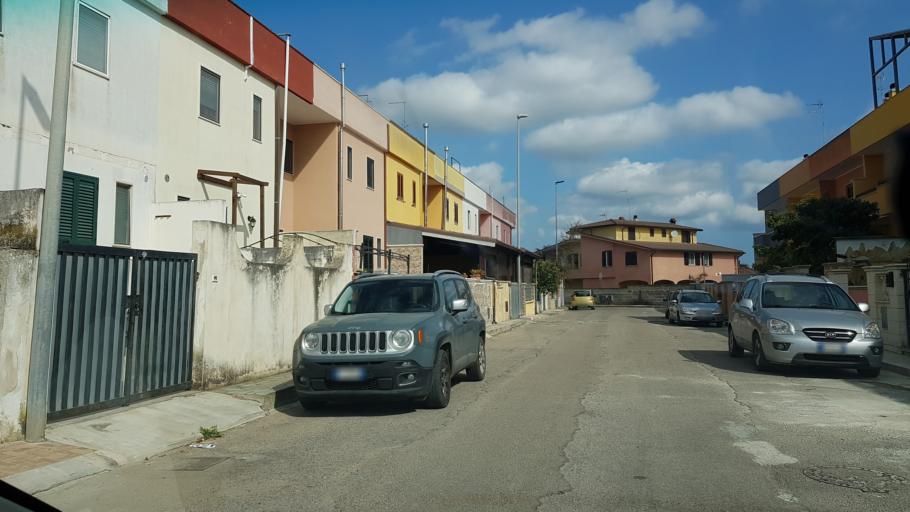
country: IT
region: Apulia
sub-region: Provincia di Brindisi
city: San Pietro Vernotico
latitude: 40.4781
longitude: 17.9998
